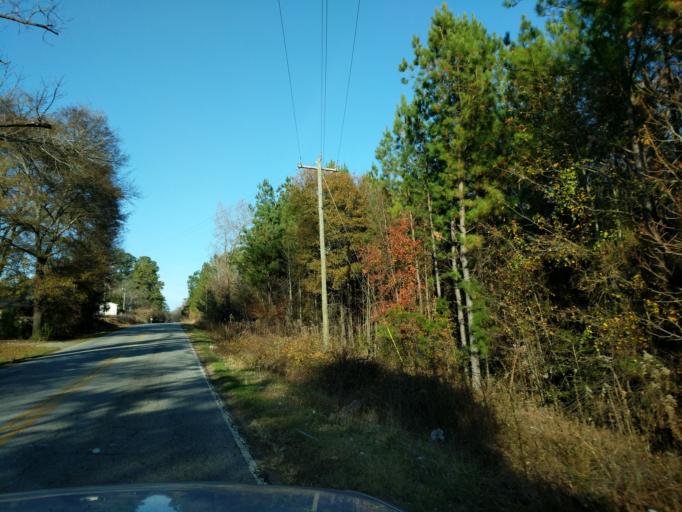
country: US
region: South Carolina
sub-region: Spartanburg County
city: Wellford
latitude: 34.9144
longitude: -82.0835
